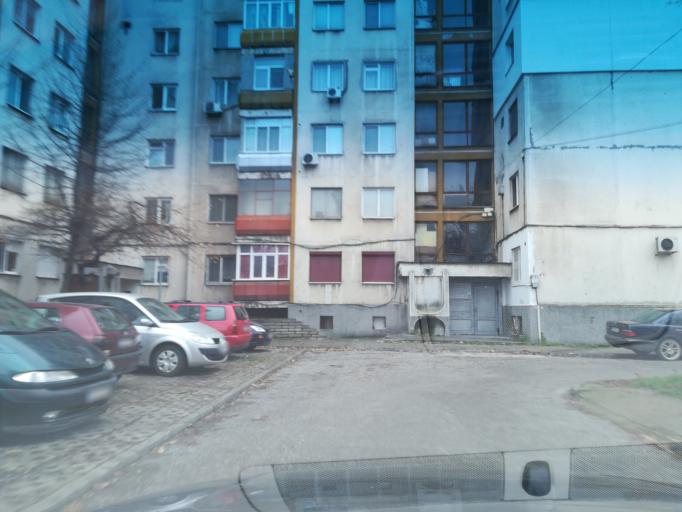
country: BG
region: Plovdiv
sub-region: Obshtina Plovdiv
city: Plovdiv
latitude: 42.1504
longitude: 24.7626
